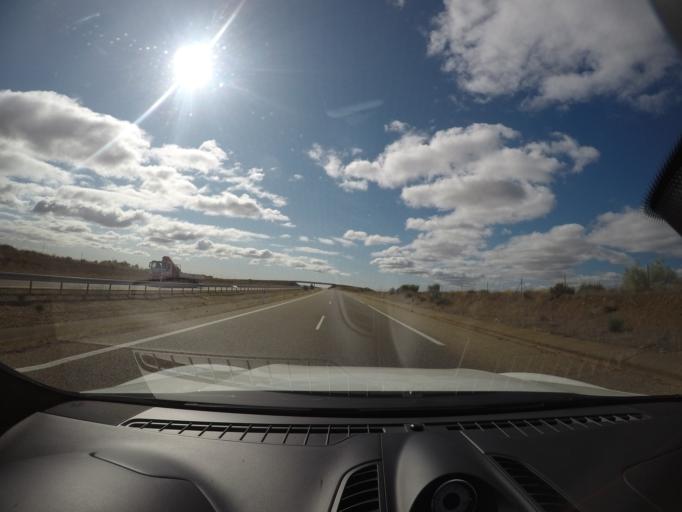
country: ES
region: Castille and Leon
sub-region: Provincia de Leon
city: Onzonilla
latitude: 42.4845
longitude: -5.5981
